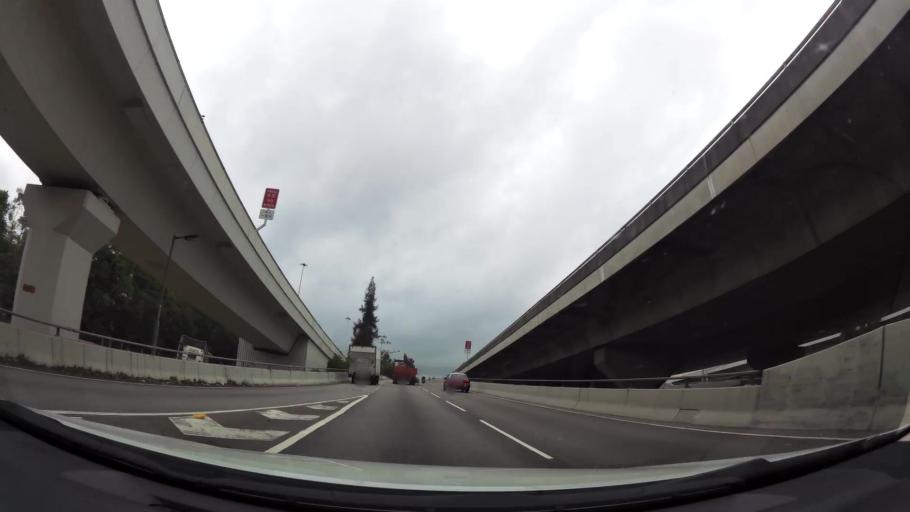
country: HK
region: Sham Shui Po
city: Sham Shui Po
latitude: 22.3318
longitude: 114.1417
